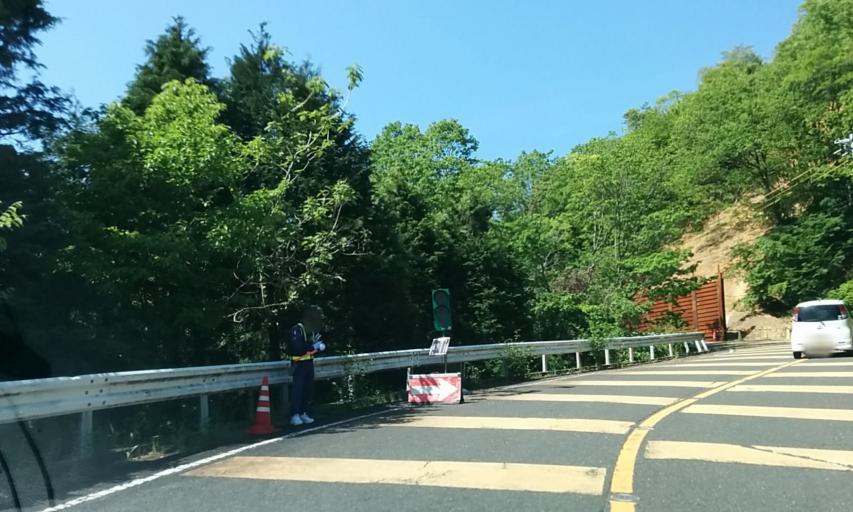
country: JP
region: Kyoto
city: Maizuru
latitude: 35.4600
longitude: 135.3520
